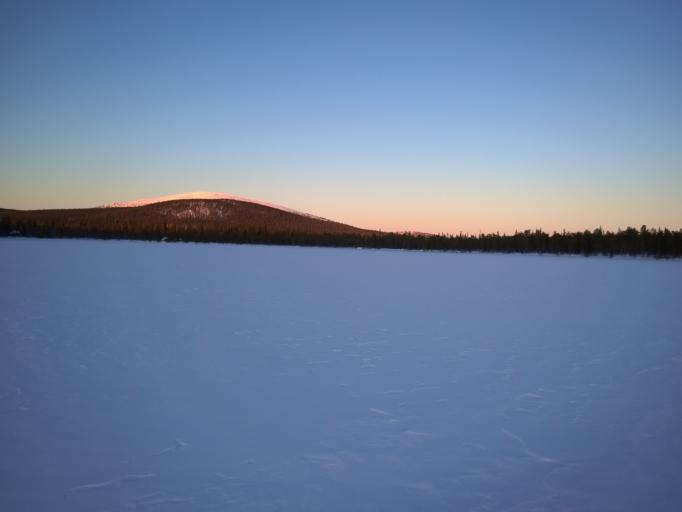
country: FI
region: Lapland
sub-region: Tunturi-Lappi
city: Muonio
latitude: 67.9322
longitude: 24.0462
